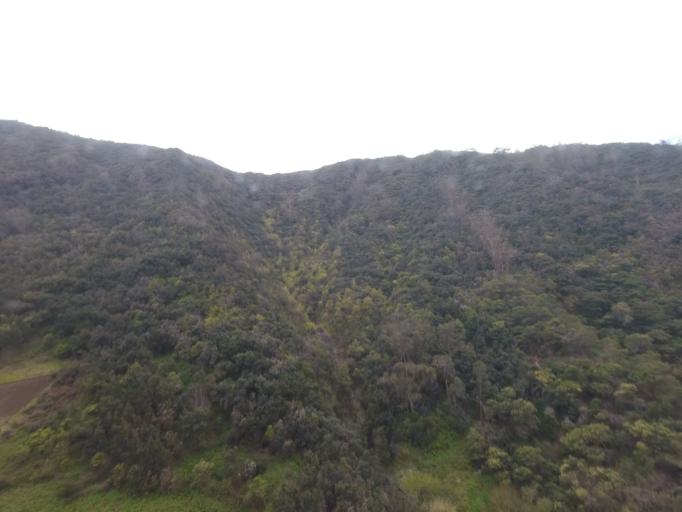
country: PT
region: Madeira
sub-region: Machico
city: Canical
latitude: 32.7615
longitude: -16.8065
